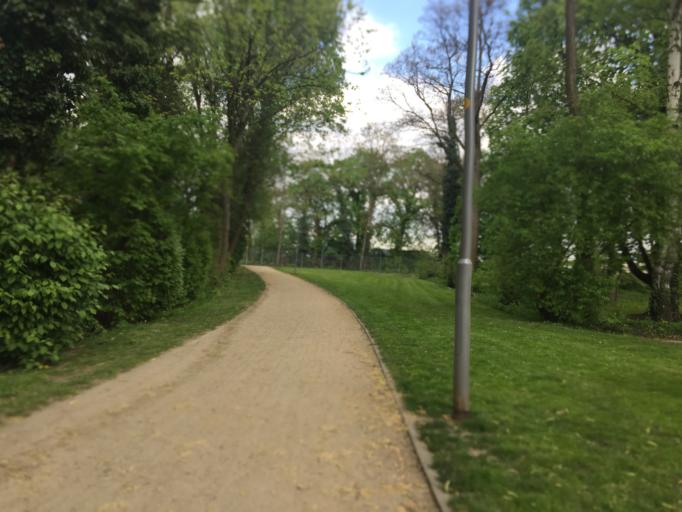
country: DE
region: Bavaria
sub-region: Regierungsbezirk Unterfranken
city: Aschaffenburg
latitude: 49.9879
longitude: 9.1482
